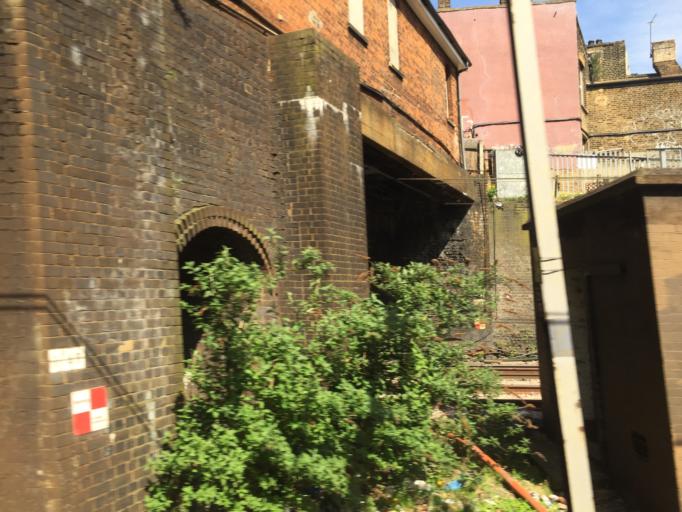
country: GB
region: England
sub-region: Greater London
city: East Ham
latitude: 51.5495
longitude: 0.0251
